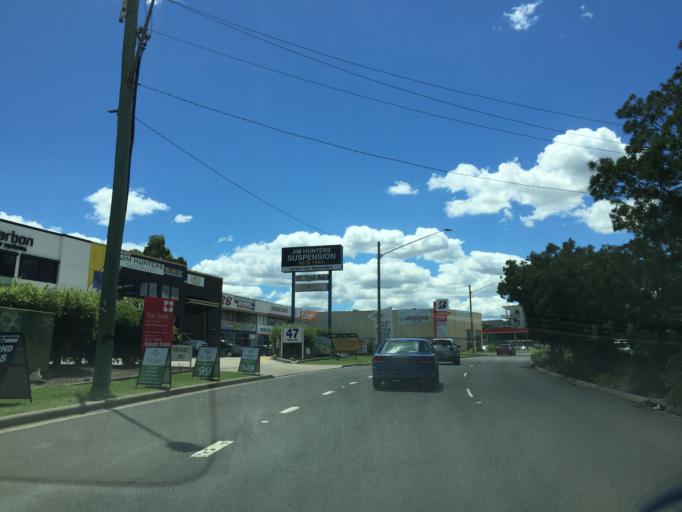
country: AU
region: New South Wales
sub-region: Blacktown
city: Blacktown
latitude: -33.7652
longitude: 150.9069
